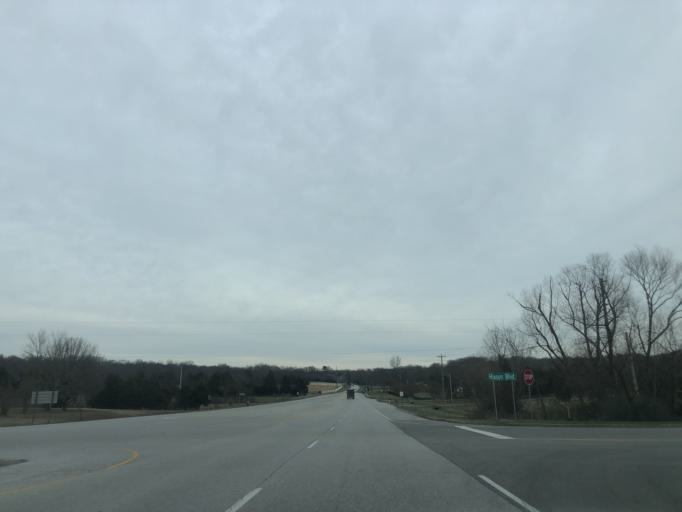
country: US
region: Tennessee
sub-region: Wilson County
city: Rural Hill
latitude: 36.1287
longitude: -86.3942
